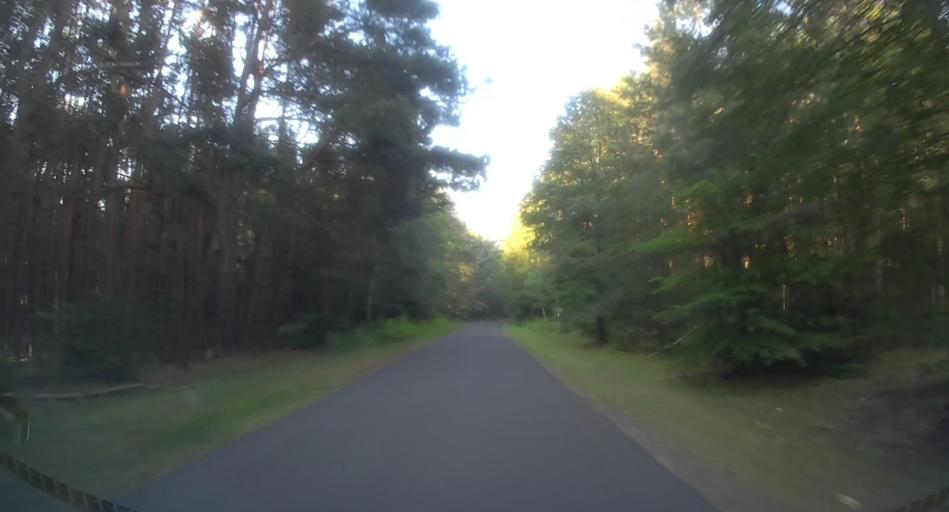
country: PL
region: Masovian Voivodeship
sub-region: Powiat zyrardowski
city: Puszcza Marianska
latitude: 51.9065
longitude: 20.3324
